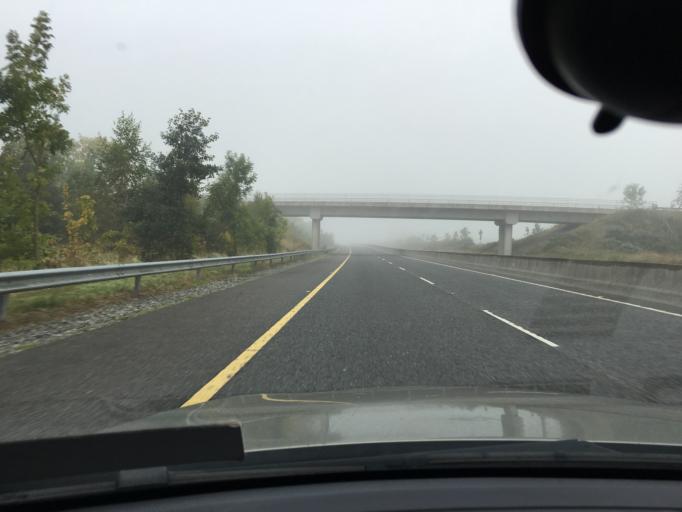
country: IE
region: Leinster
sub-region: Uibh Fhaili
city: Clara
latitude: 53.3793
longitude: -7.5644
